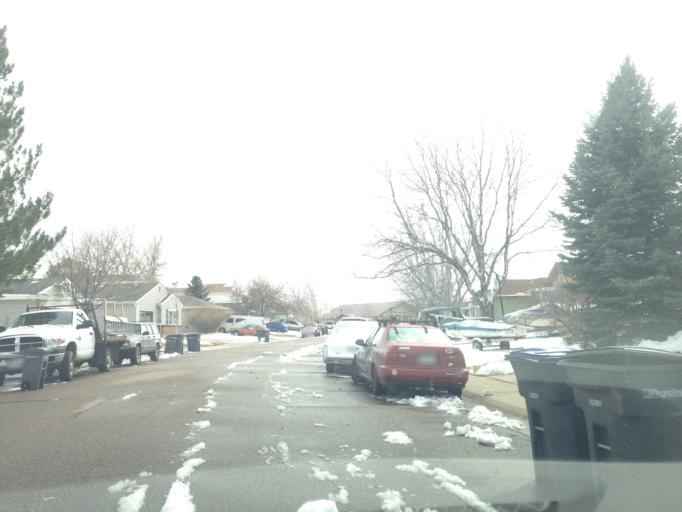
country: US
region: Colorado
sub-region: Boulder County
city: Lafayette
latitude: 39.9750
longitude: -105.0924
